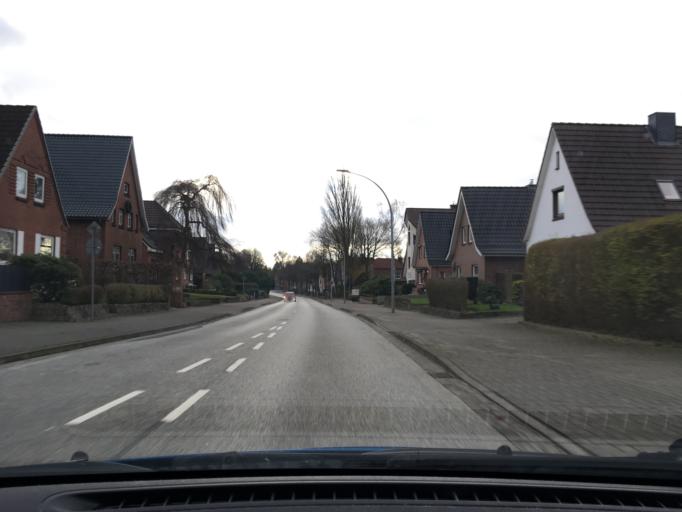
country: DE
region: Schleswig-Holstein
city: Heiligenstedten
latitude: 53.9405
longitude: 9.4972
